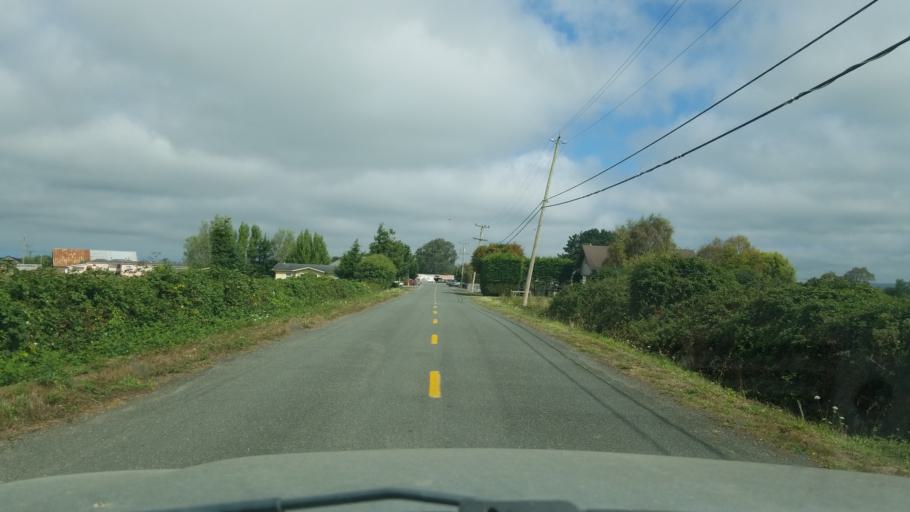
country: US
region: California
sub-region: Humboldt County
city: Ferndale
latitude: 40.5919
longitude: -124.2553
